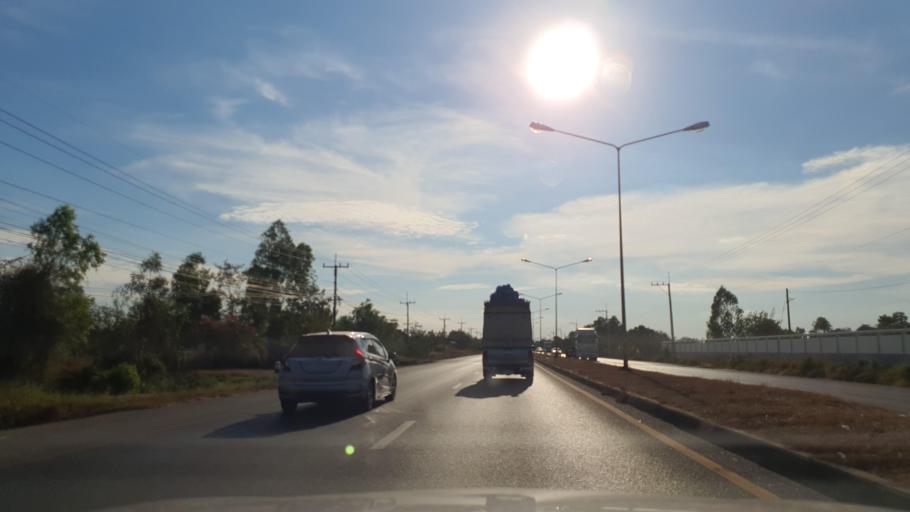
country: TH
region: Maha Sarakham
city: Kantharawichai
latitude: 16.3551
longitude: 103.3320
